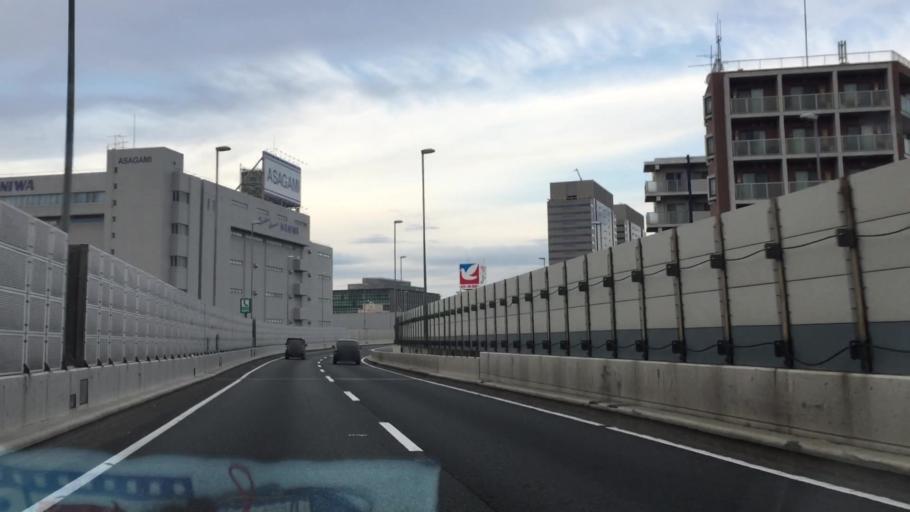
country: JP
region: Tokyo
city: Urayasu
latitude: 35.6620
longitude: 139.8059
